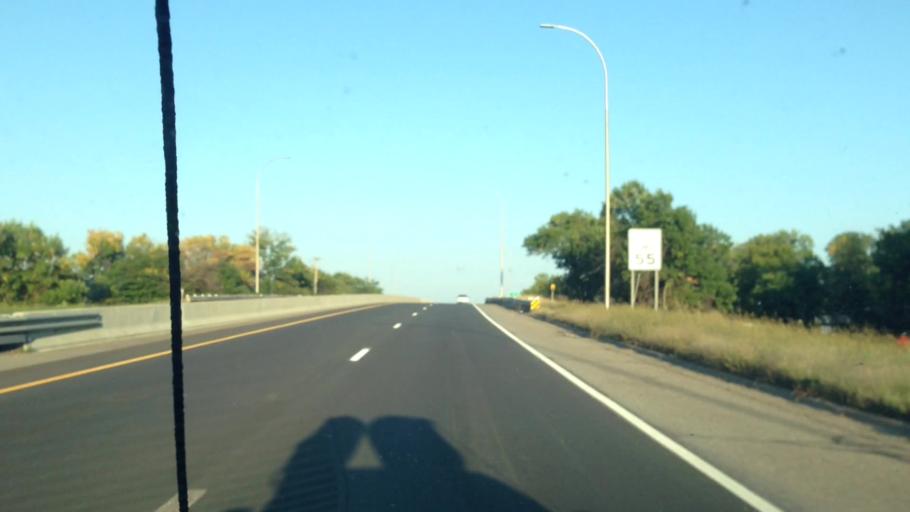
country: US
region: Minnesota
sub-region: Hennepin County
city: Richfield
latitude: 44.8973
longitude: -93.2343
